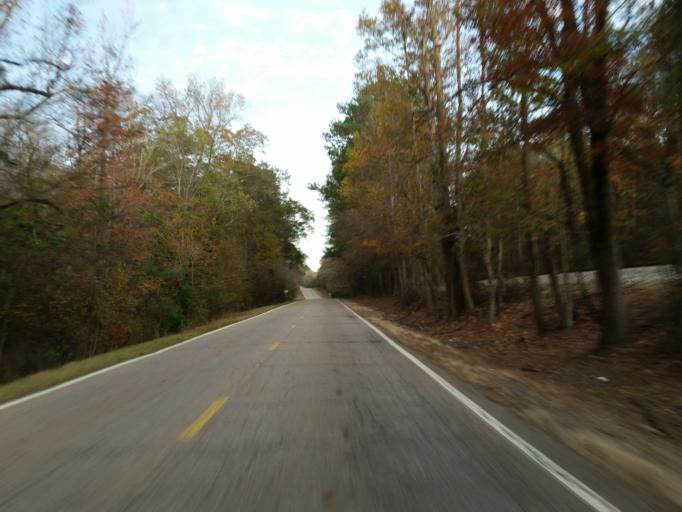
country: US
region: Alabama
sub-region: Sumter County
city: York
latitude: 32.4239
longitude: -88.4265
